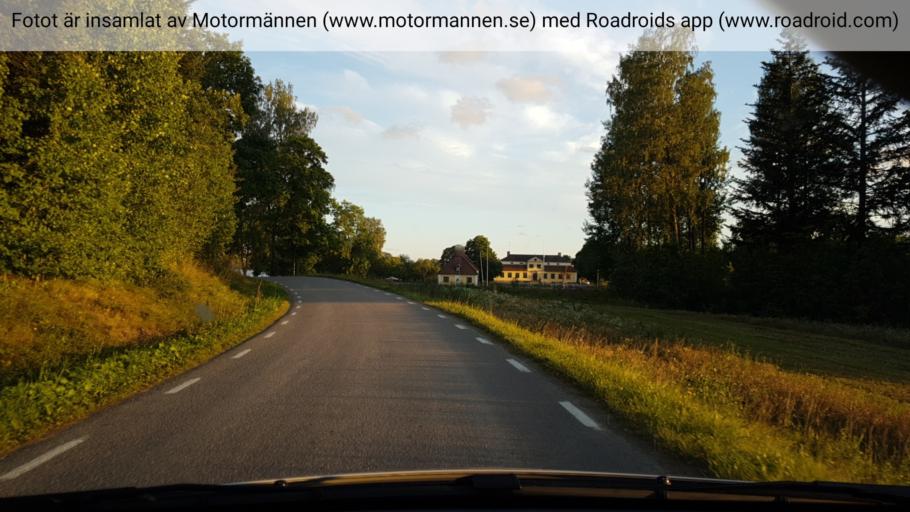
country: SE
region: Vaestmanland
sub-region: Surahammars Kommun
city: Ramnas
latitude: 59.6973
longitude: 16.0658
